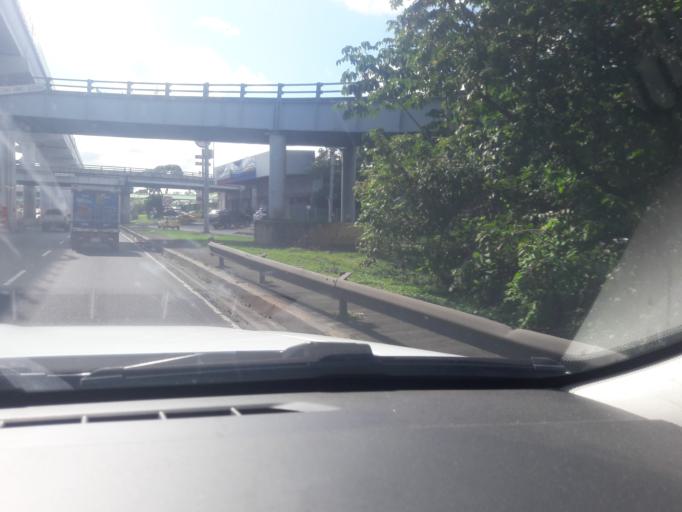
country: PA
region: Panama
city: San Miguelito
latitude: 9.0504
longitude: -79.4532
